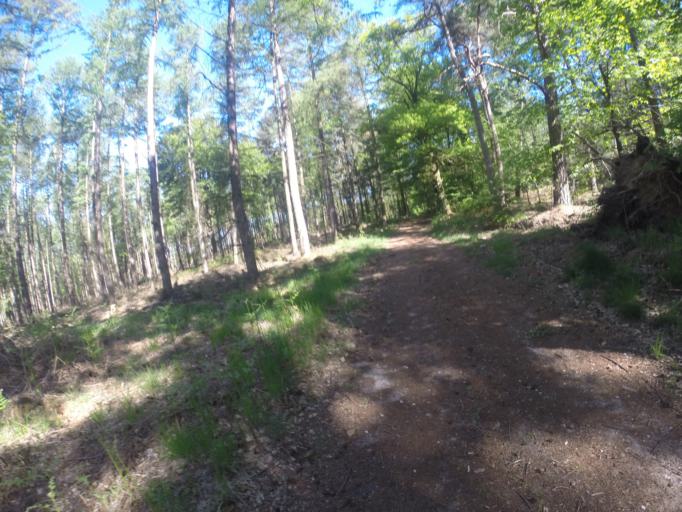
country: NL
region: Gelderland
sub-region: Gemeente Montferland
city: s-Heerenberg
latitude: 51.9132
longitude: 6.2284
